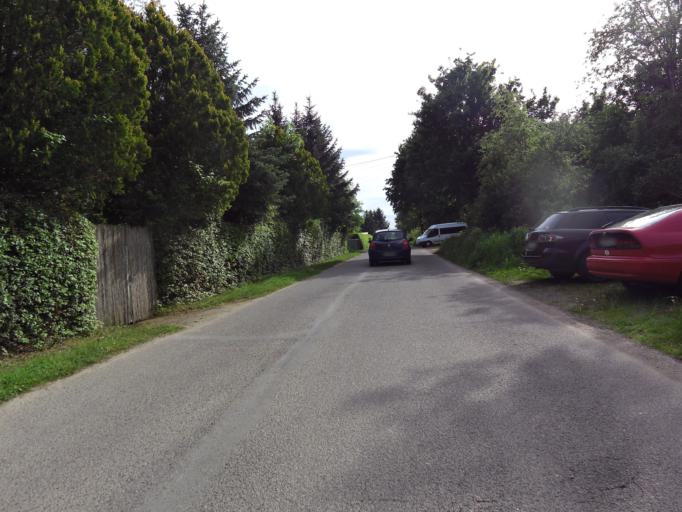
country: DE
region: Saxony
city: Markkleeberg
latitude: 51.2995
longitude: 12.3119
